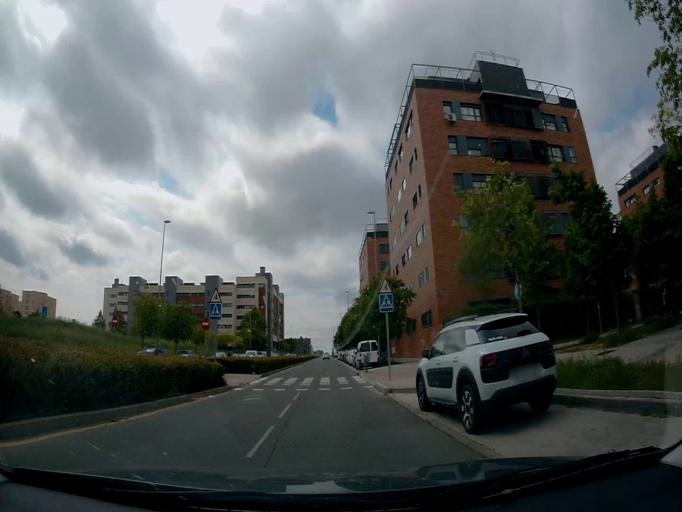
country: ES
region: Madrid
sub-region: Provincia de Madrid
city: Alcorcon
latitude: 40.3326
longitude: -3.8350
